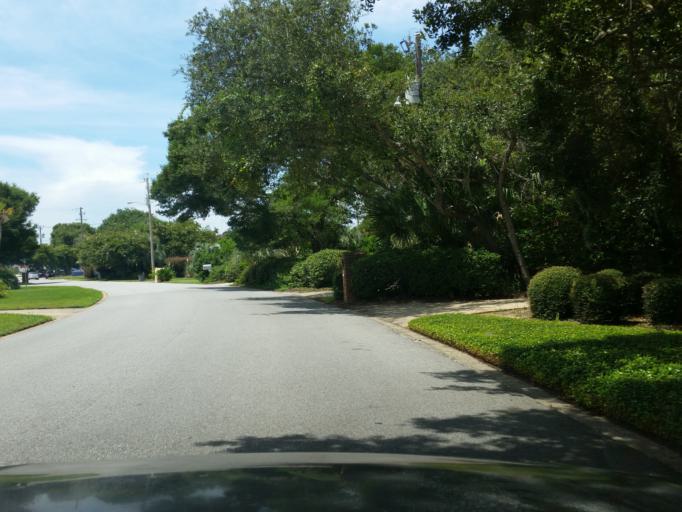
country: US
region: Florida
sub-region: Santa Rosa County
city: Gulf Breeze
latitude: 30.3670
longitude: -87.1673
